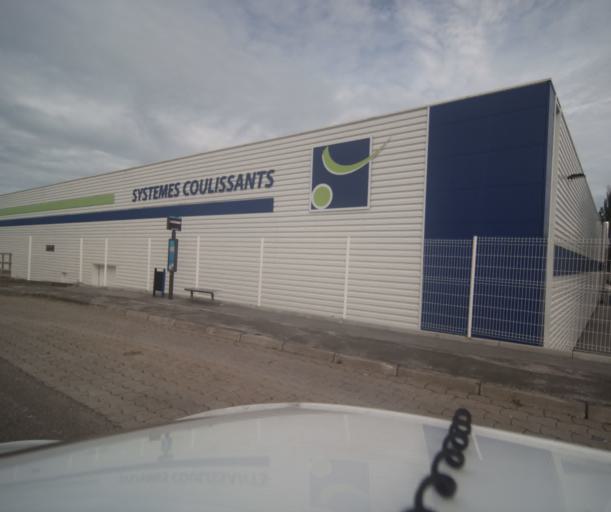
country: FR
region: Franche-Comte
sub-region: Departement du Doubs
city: Besancon
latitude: 47.2385
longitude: 5.9887
